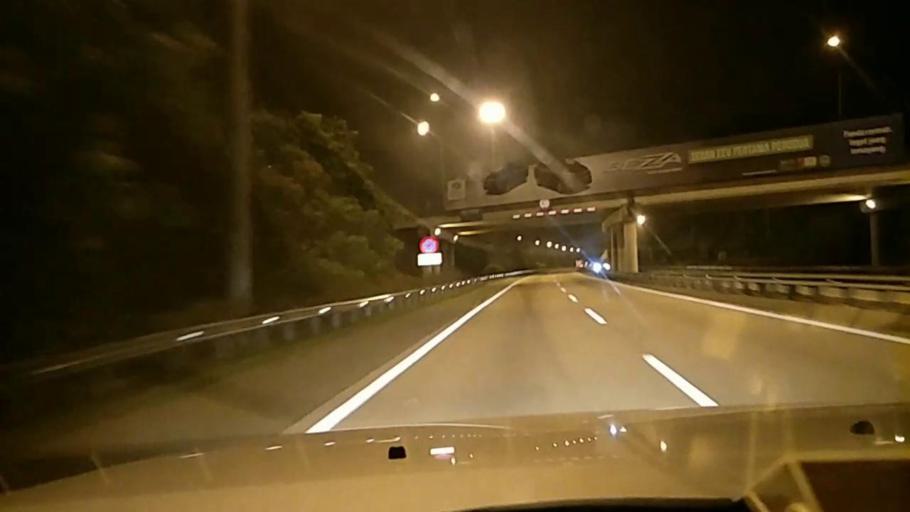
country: MY
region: Perak
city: Bidur
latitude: 3.9889
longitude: 101.3204
